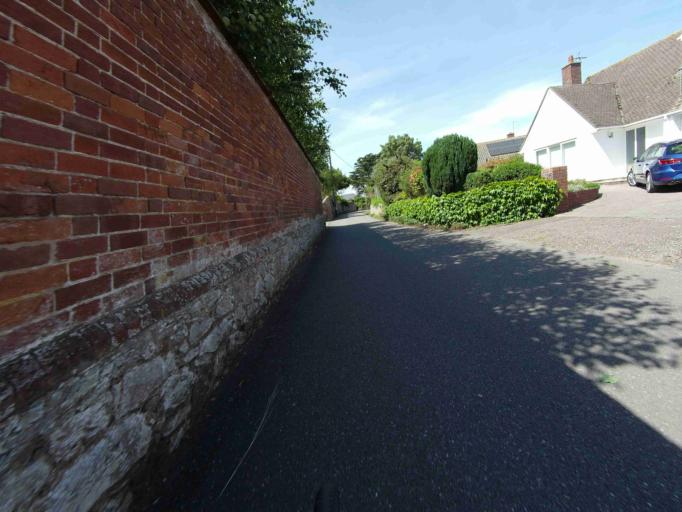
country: GB
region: England
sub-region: Devon
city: Starcross
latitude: 50.6452
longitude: -3.4308
